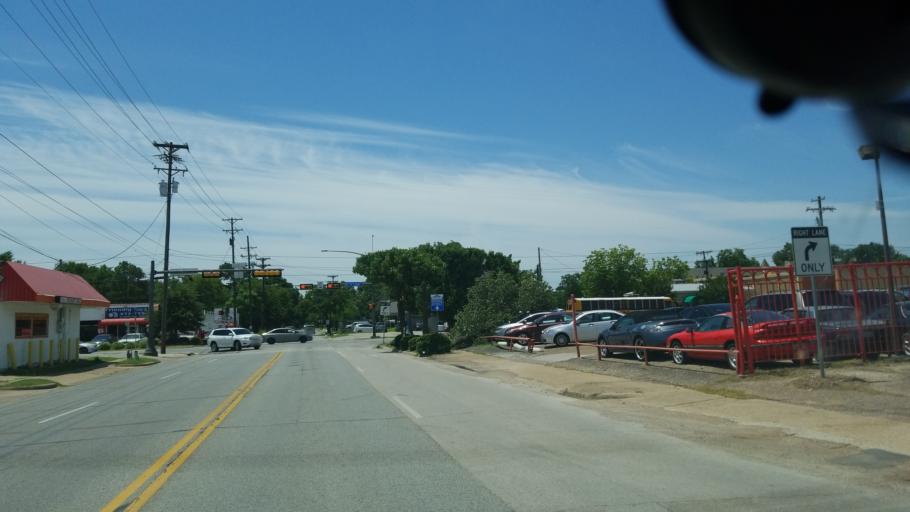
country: US
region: Texas
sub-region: Dallas County
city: Irving
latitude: 32.8144
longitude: -96.9425
